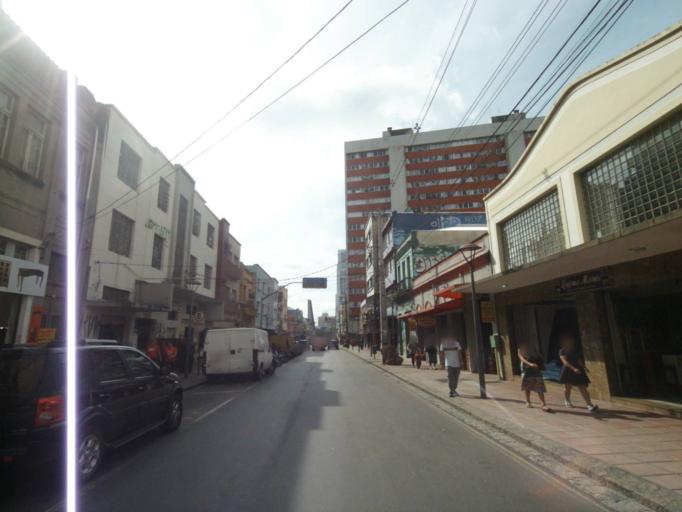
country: BR
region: Parana
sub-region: Curitiba
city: Curitiba
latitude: -25.4280
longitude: -49.2694
